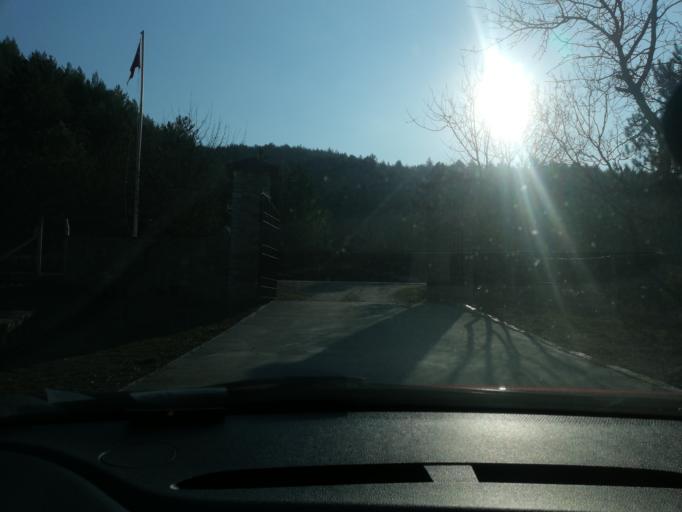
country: TR
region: Karabuk
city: Safranbolu
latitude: 41.2129
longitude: 32.7501
